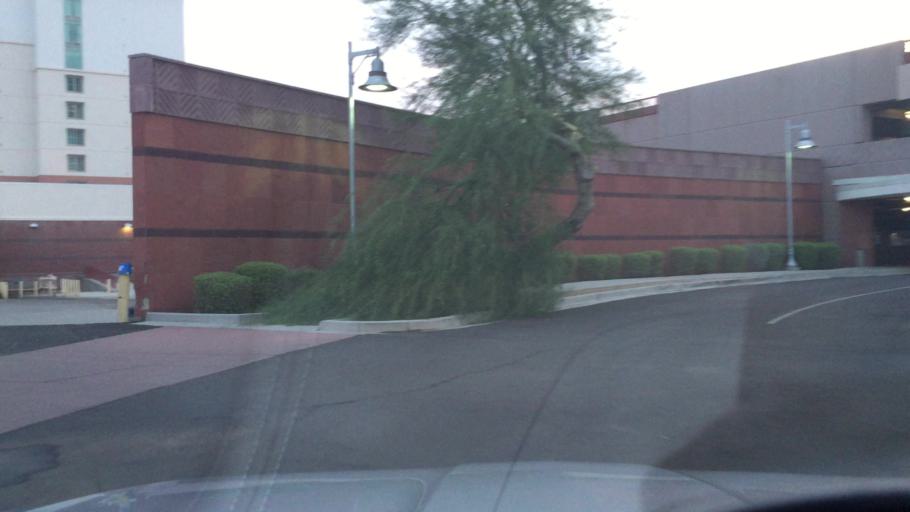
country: US
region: Arizona
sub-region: Maricopa County
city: Peoria
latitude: 33.5313
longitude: -112.2632
